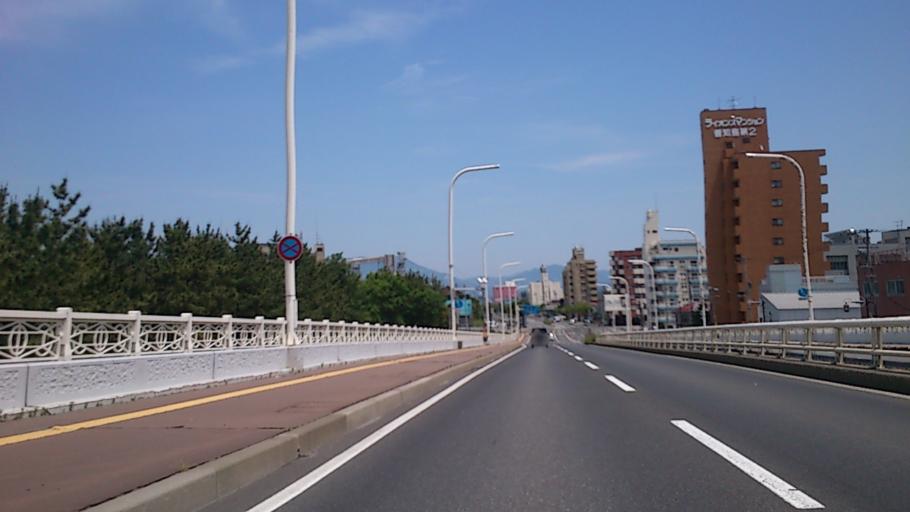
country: JP
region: Aomori
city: Aomori Shi
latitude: 40.8290
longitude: 140.7425
